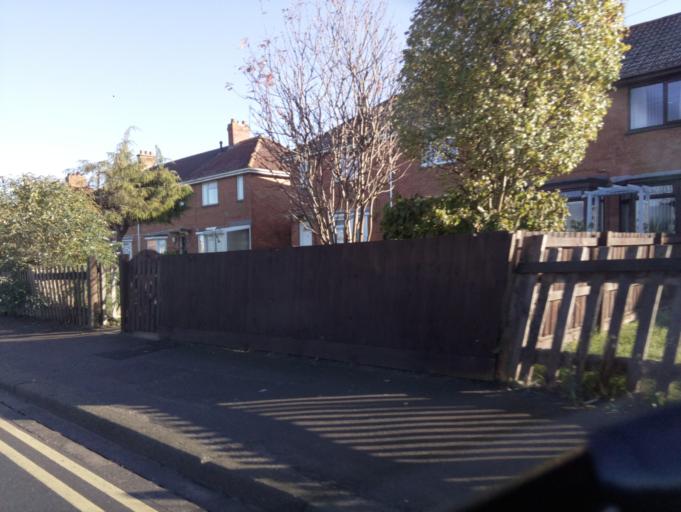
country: GB
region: England
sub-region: Somerset
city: Bridgwater
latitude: 51.1363
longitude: -2.9936
